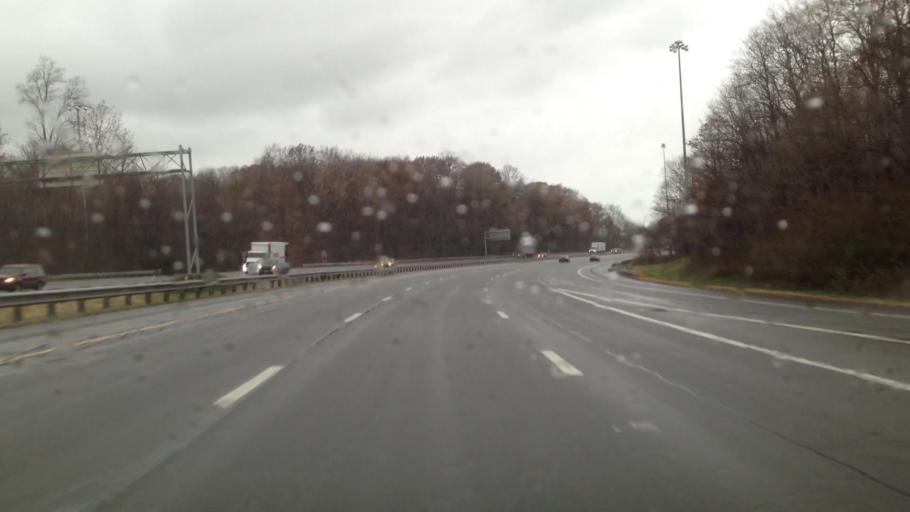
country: US
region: Ohio
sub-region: Lake County
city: Wickliffe
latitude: 41.5906
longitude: -81.4832
